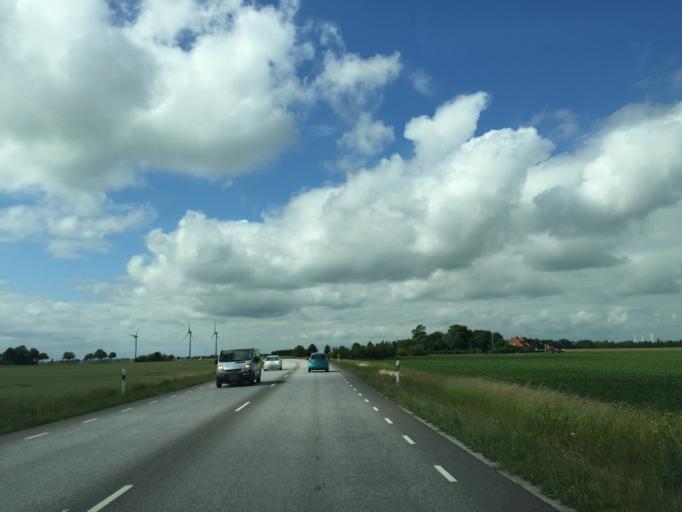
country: SE
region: Skane
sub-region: Staffanstorps Kommun
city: Hjaerup
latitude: 55.6902
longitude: 13.1504
